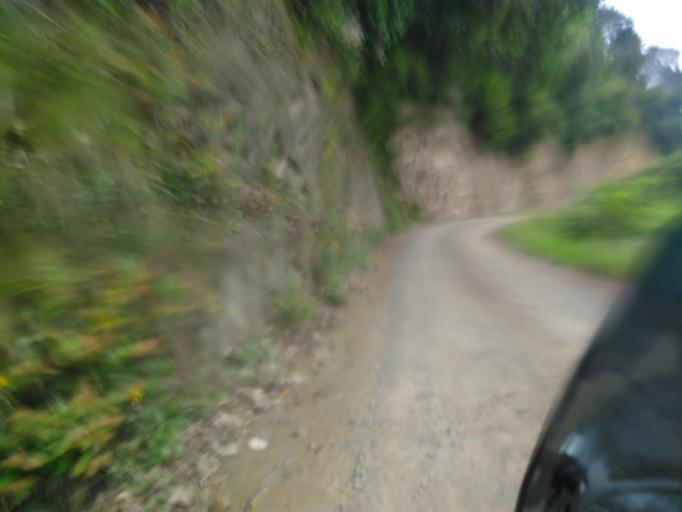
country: NZ
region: Bay of Plenty
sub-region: Opotiki District
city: Opotiki
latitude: -38.0326
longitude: 177.4406
